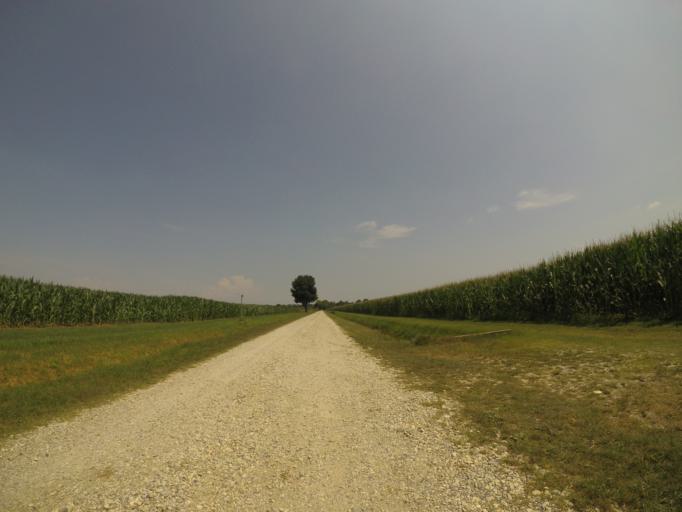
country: IT
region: Friuli Venezia Giulia
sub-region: Provincia di Udine
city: Codroipo
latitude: 45.9483
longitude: 12.9959
